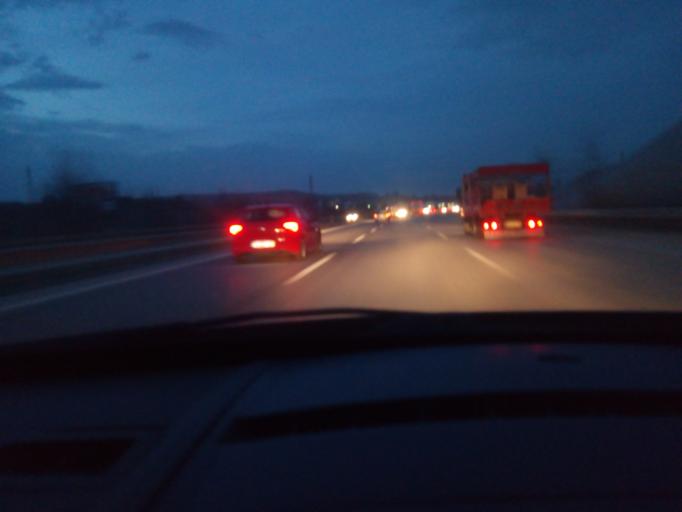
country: TR
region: Balikesir
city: Susurluk
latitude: 39.9610
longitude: 28.1705
